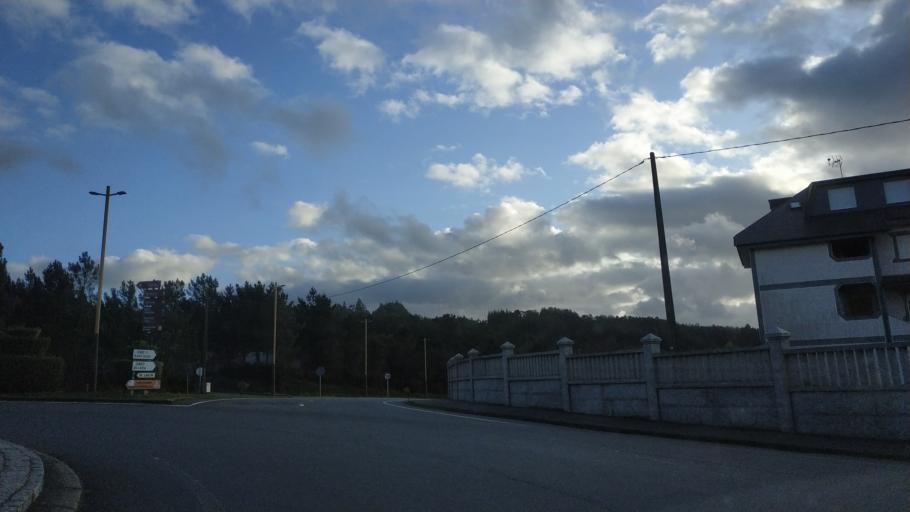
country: ES
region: Galicia
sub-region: Provincia de Pontevedra
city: Silleda
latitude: 42.7926
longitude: -8.1612
